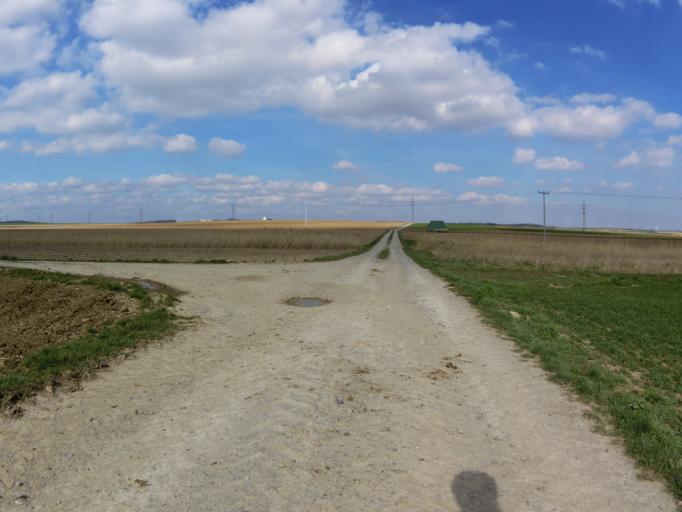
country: DE
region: Bavaria
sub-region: Regierungsbezirk Unterfranken
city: Biebelried
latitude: 49.7483
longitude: 10.0809
